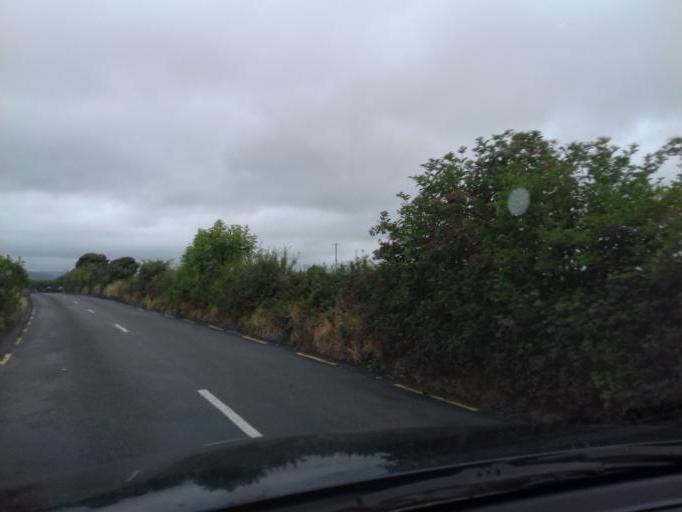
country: IE
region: Leinster
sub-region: County Carlow
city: Bagenalstown
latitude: 52.7174
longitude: -6.9628
